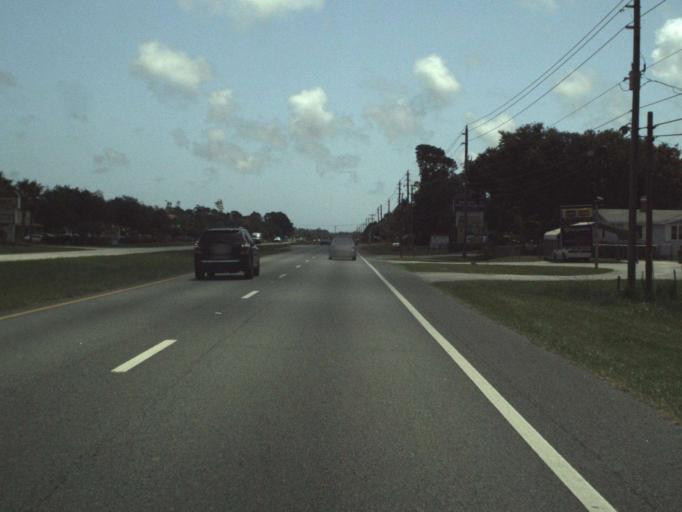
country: US
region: Florida
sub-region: Volusia County
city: Ormond-by-the-Sea
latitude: 29.3313
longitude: -81.1250
